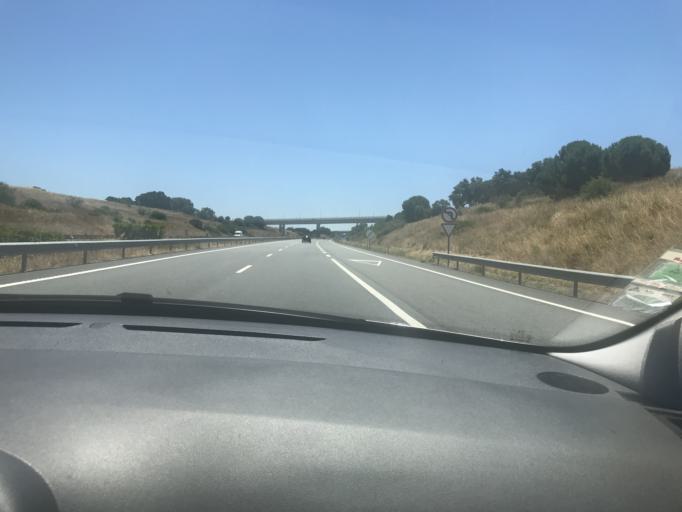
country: PT
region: Setubal
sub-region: Grandola
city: Grandola
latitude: 38.1233
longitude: -8.4118
